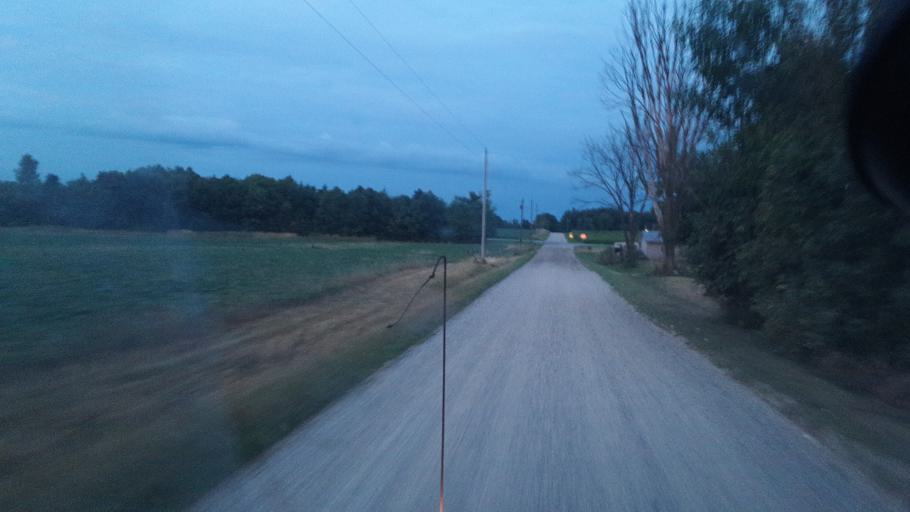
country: US
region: Ohio
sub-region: Defiance County
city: Hicksville
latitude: 41.3427
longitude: -84.8305
